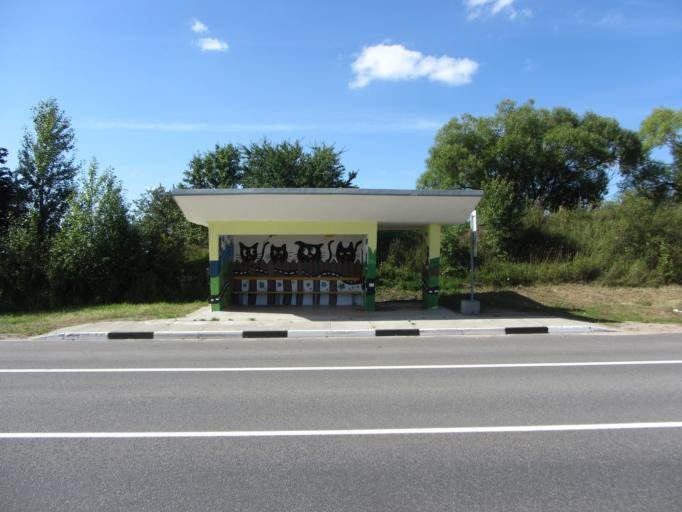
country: LT
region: Utenos apskritis
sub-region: Utena
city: Utena
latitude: 55.5265
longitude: 25.6790
